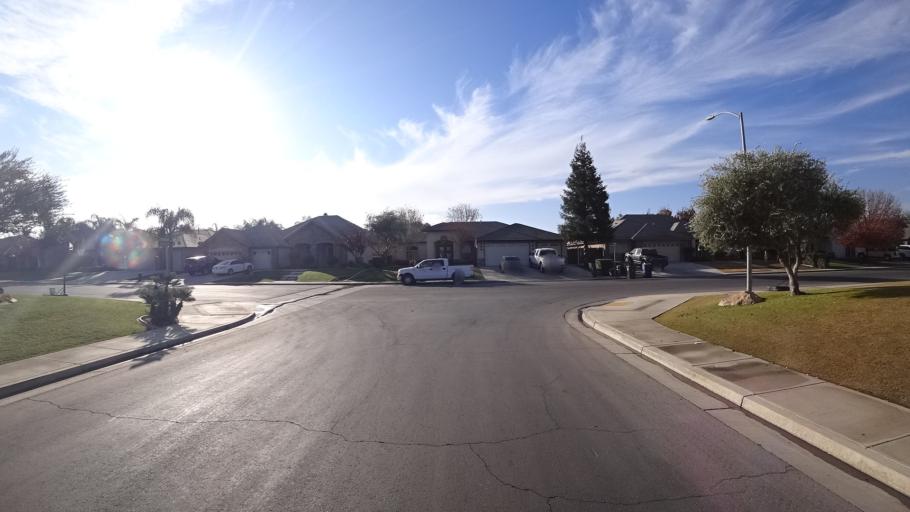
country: US
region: California
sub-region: Kern County
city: Rosedale
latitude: 35.4095
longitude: -119.1338
